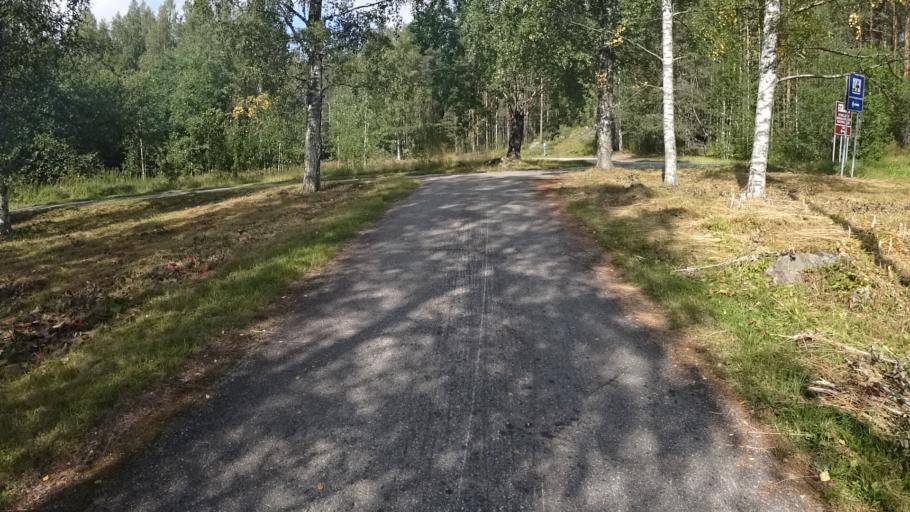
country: FI
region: North Karelia
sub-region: Joensuu
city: Ilomantsi
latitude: 62.6223
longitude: 31.1968
